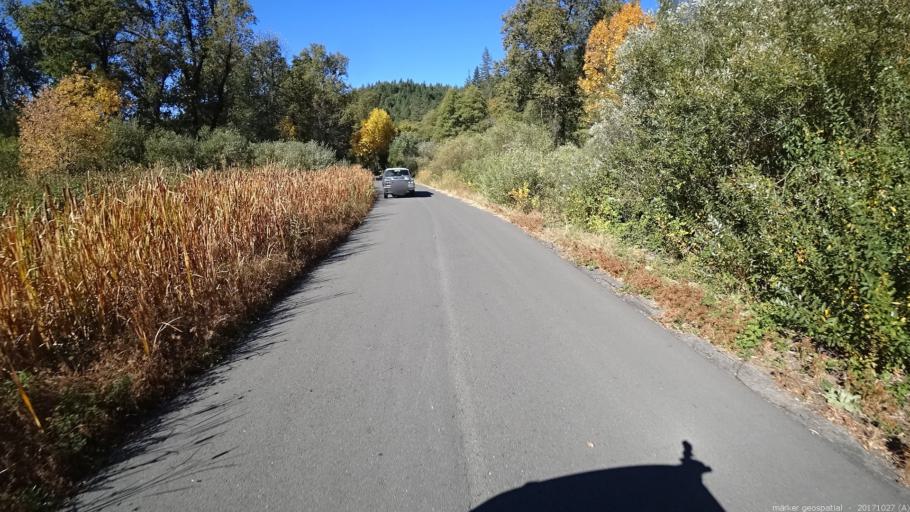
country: US
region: California
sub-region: Shasta County
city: Bella Vista
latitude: 40.7547
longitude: -122.0237
